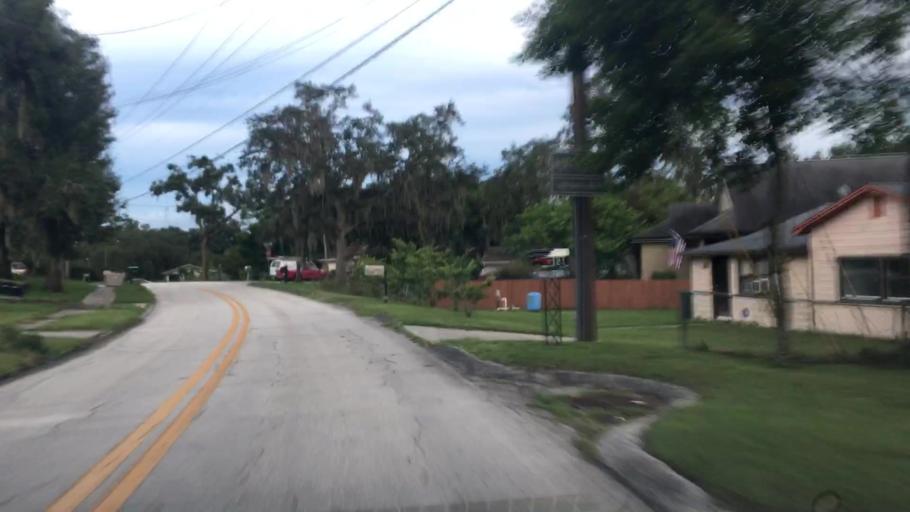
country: US
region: Florida
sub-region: Volusia County
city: DeBary
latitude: 28.8792
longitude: -81.3044
